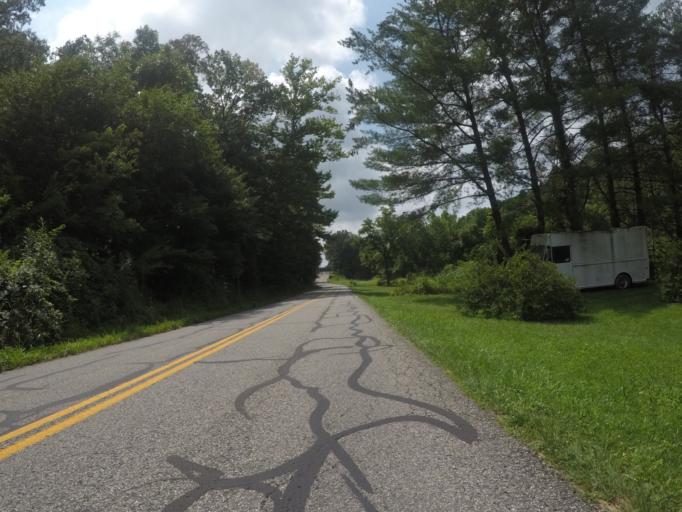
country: US
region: Kentucky
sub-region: Boyd County
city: Meads
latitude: 38.4047
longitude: -82.6597
